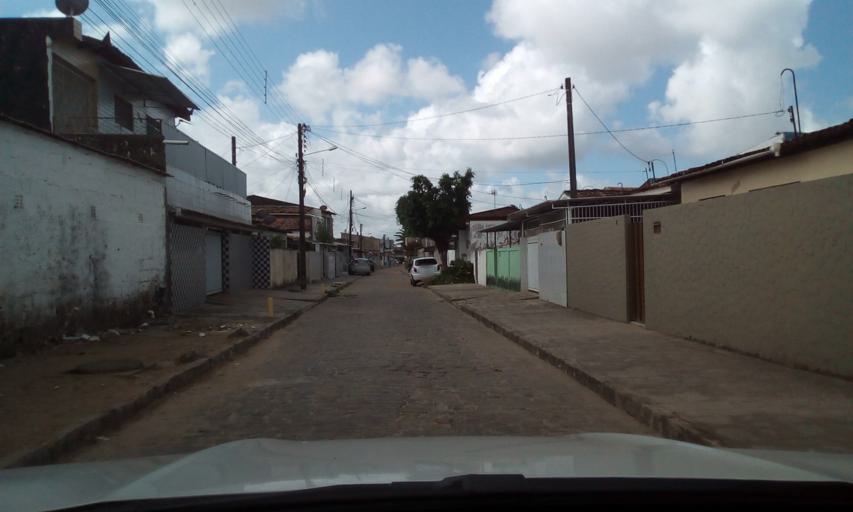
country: BR
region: Paraiba
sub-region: Joao Pessoa
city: Joao Pessoa
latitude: -7.1524
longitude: -34.8733
